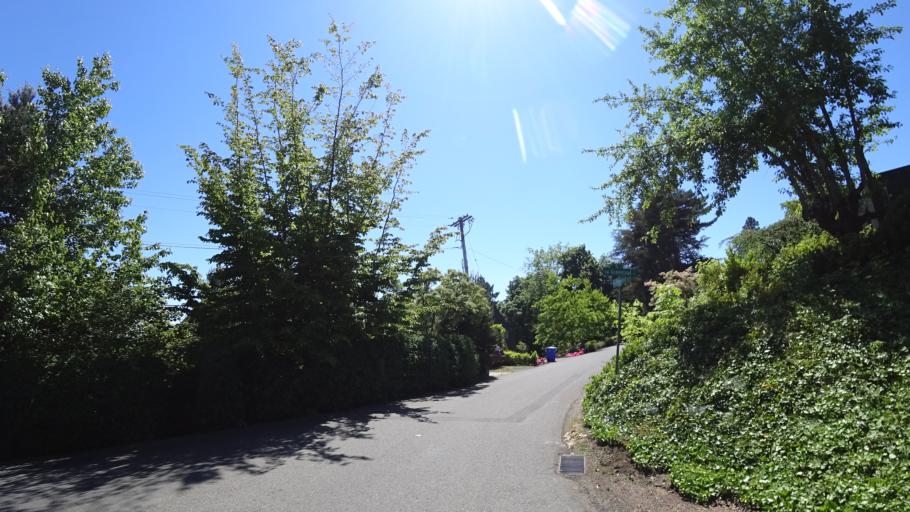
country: US
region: Oregon
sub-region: Washington County
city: West Slope
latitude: 45.5023
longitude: -122.7183
